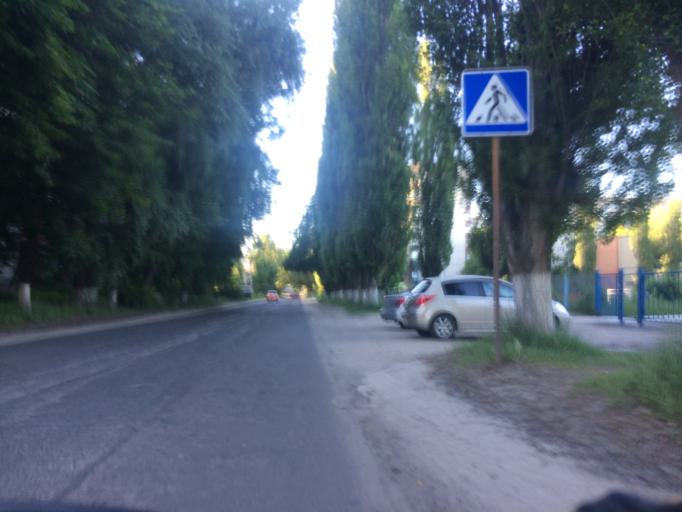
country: RU
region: Kursk
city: Kursk
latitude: 51.6718
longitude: 36.1540
